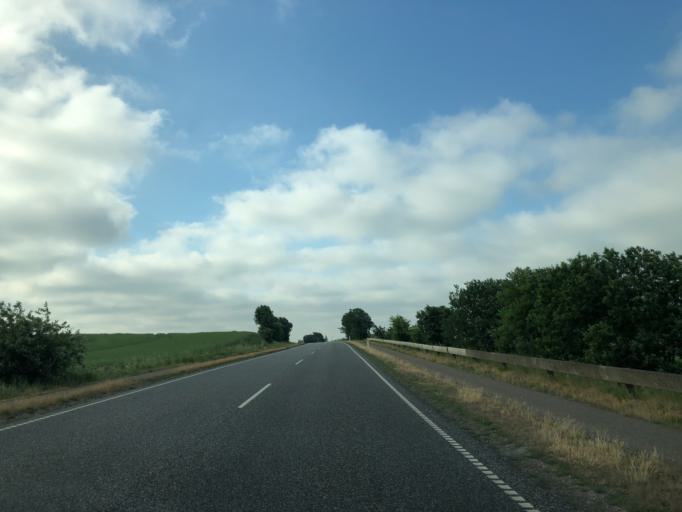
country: DK
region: South Denmark
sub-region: Vejle Kommune
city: Jelling
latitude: 55.7317
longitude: 9.3578
